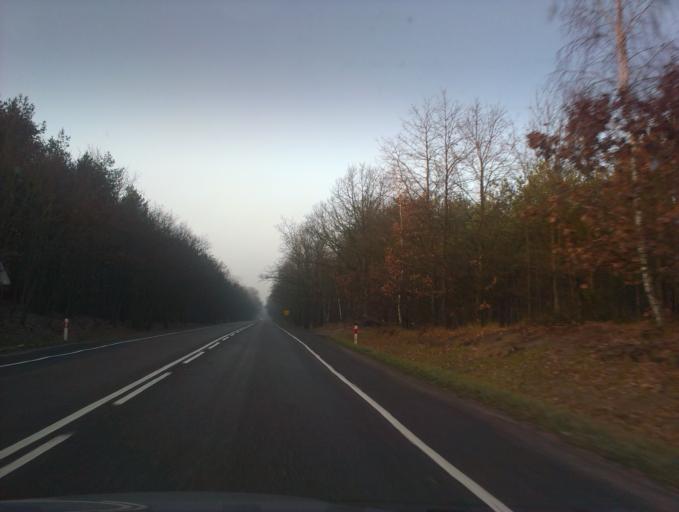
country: PL
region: Greater Poland Voivodeship
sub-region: Powiat obornicki
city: Rogozno
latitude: 52.7229
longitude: 16.9289
